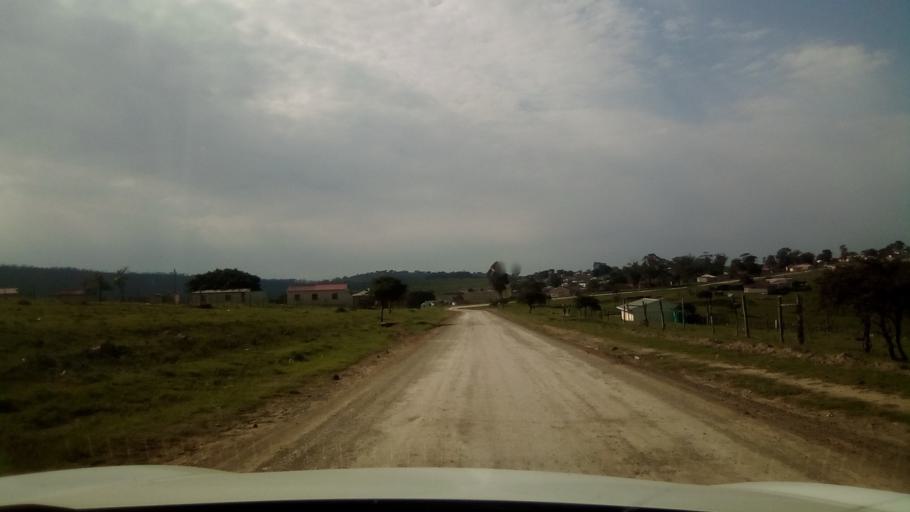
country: ZA
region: Eastern Cape
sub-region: Buffalo City Metropolitan Municipality
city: Bhisho
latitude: -32.9858
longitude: 27.2612
